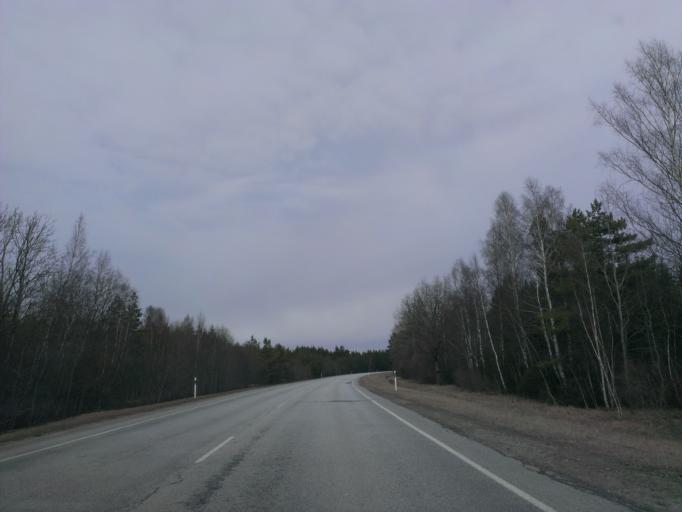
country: EE
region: Laeaene
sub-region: Lihula vald
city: Lihula
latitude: 58.6016
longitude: 23.5542
